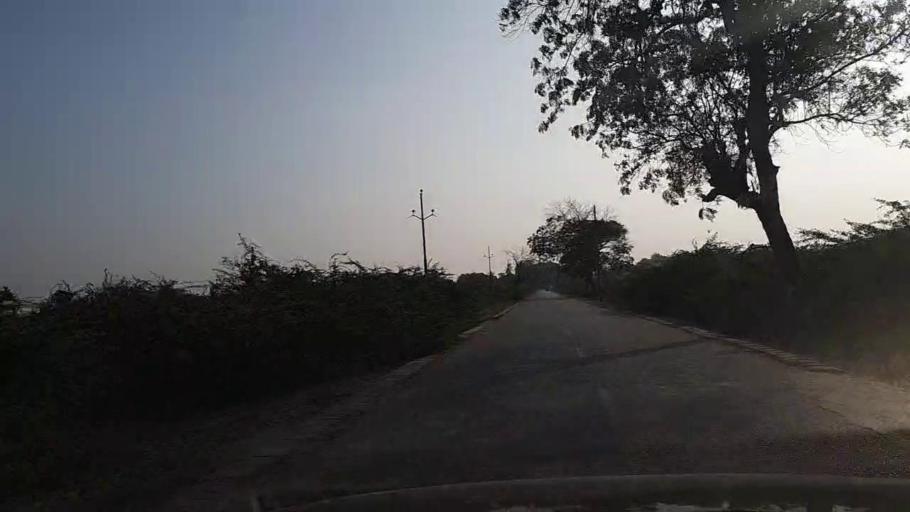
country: PK
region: Sindh
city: Gharo
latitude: 24.7807
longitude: 67.5112
